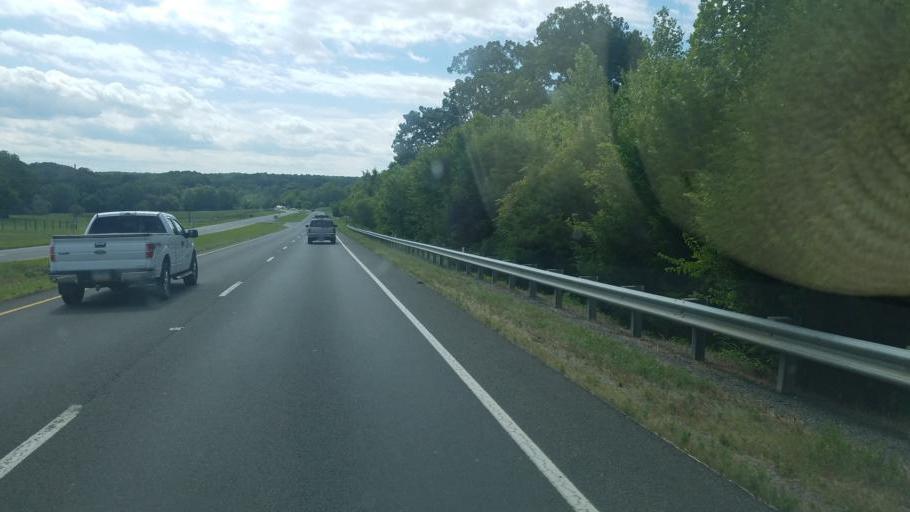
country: US
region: Virginia
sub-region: Fauquier County
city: Bealeton
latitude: 38.4354
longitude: -77.6374
